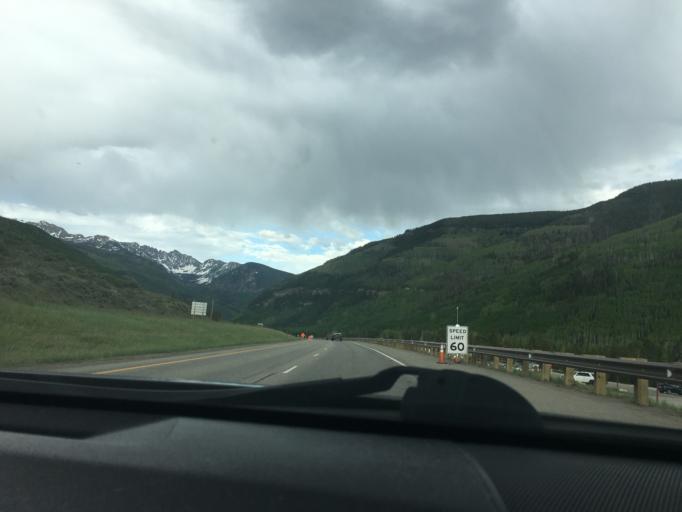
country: US
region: Colorado
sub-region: Eagle County
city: Vail
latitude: 39.6413
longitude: -106.3642
